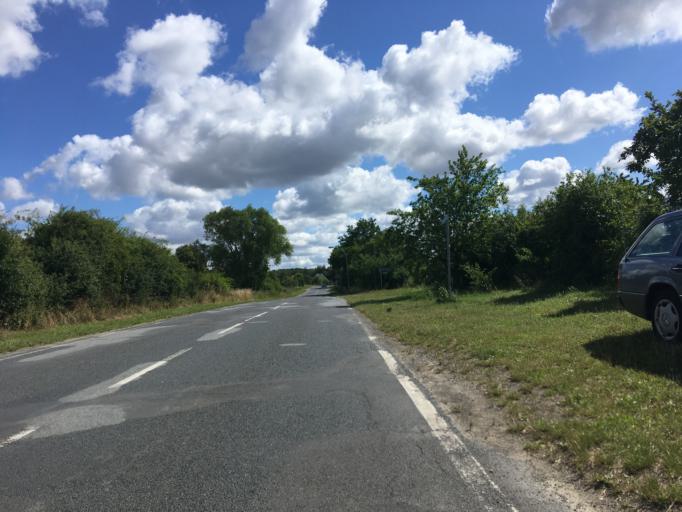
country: DE
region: Brandenburg
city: Mittenwalde
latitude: 53.1937
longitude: 13.5961
